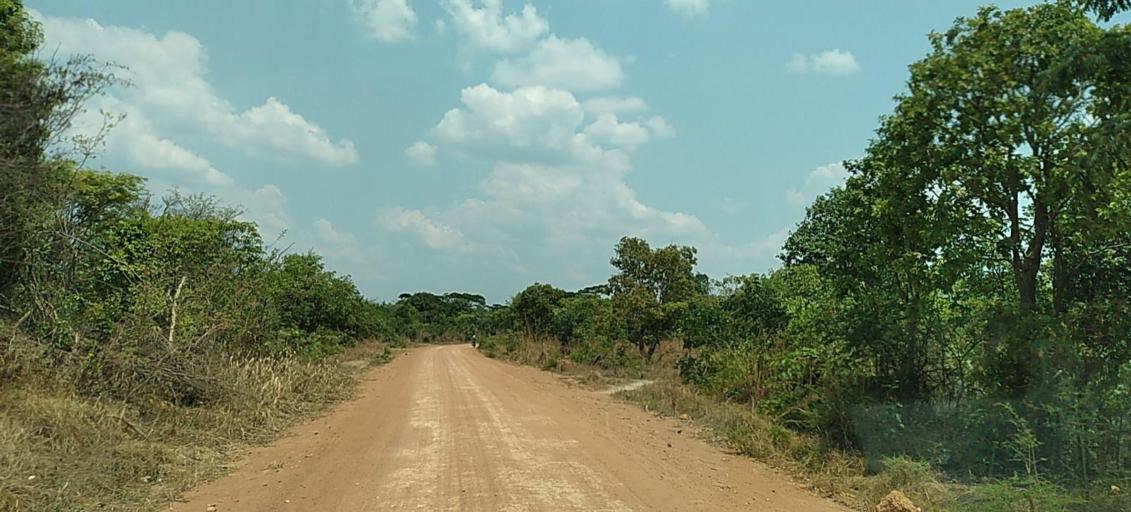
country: ZM
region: Copperbelt
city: Luanshya
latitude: -13.1414
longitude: 28.3156
